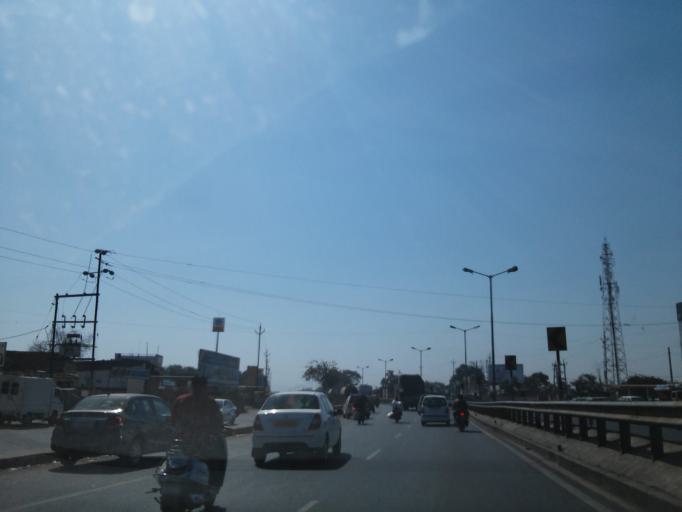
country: IN
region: Gujarat
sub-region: Sabar Kantha
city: Himatnagar
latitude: 23.5805
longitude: 72.9586
